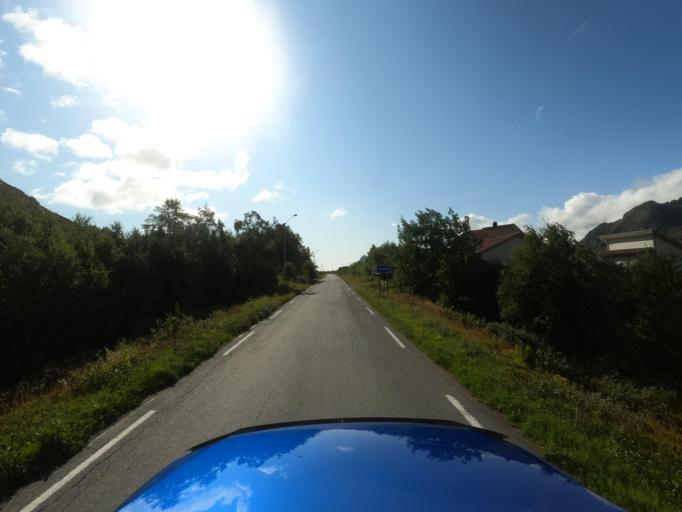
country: NO
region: Nordland
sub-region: Vestvagoy
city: Evjen
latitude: 68.1326
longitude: 13.7800
